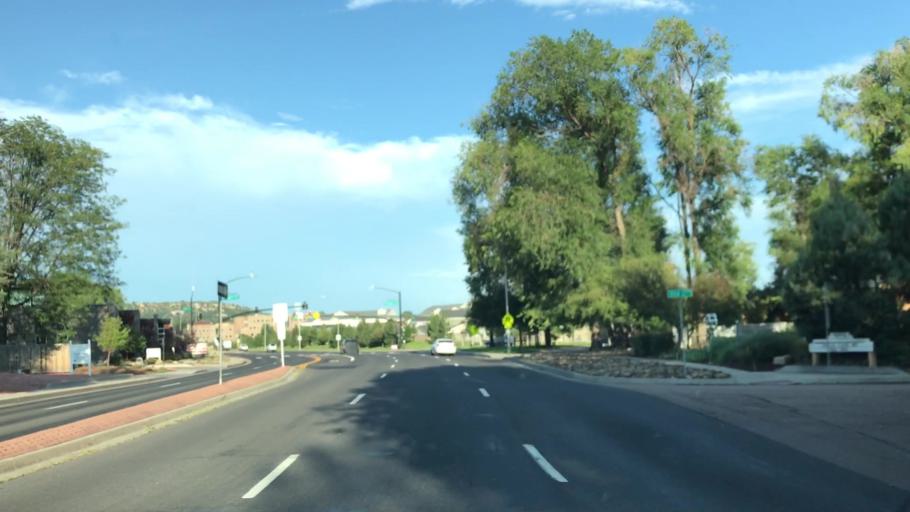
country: US
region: Colorado
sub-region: El Paso County
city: Colorado Springs
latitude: 38.8737
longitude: -104.8010
